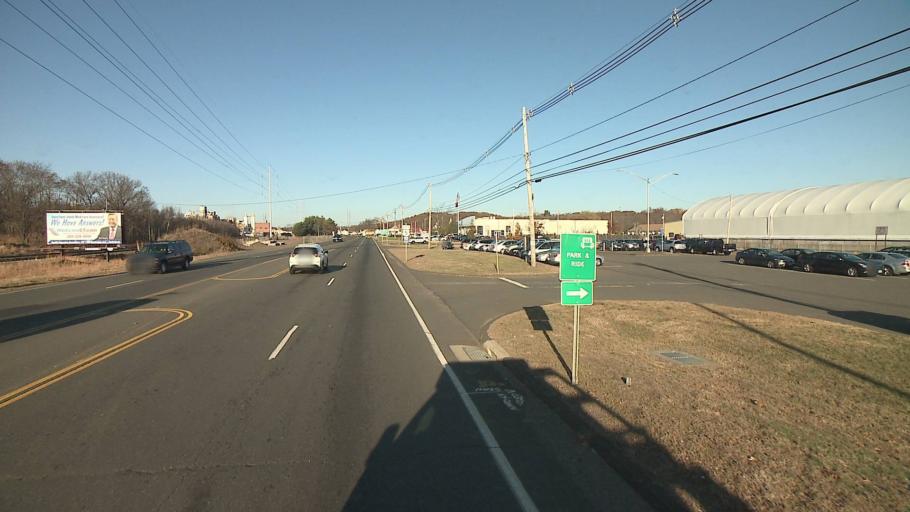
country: US
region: Connecticut
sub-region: New Haven County
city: Wallingford Center
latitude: 41.4299
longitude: -72.8365
